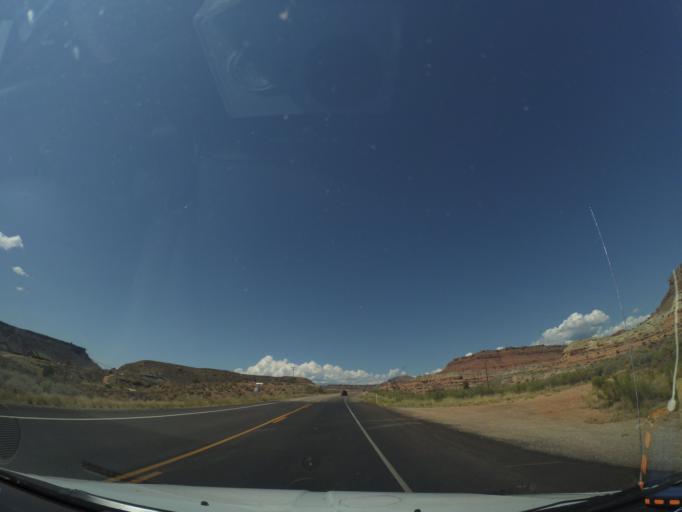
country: US
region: Utah
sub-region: Washington County
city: Hildale
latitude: 37.1637
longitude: -113.0596
